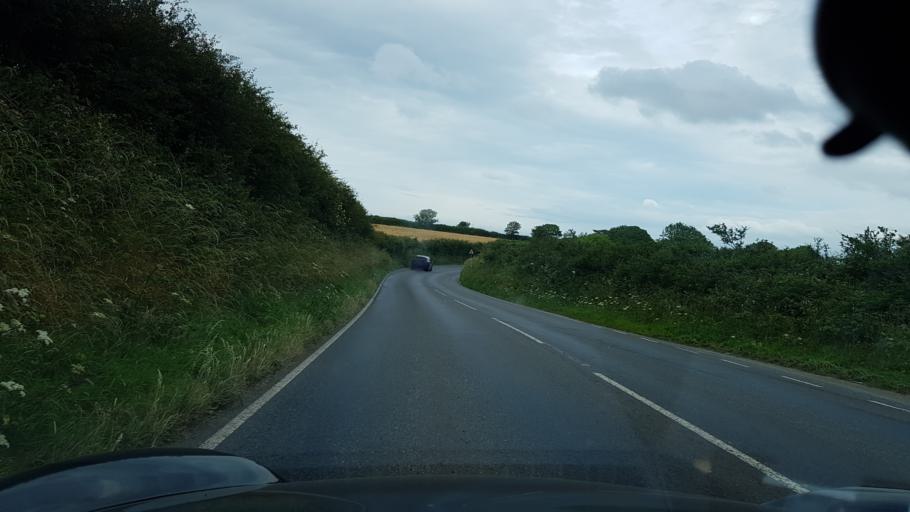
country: GB
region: Wales
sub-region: Pembrokeshire
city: Herbrandston
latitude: 51.7715
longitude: -5.0599
